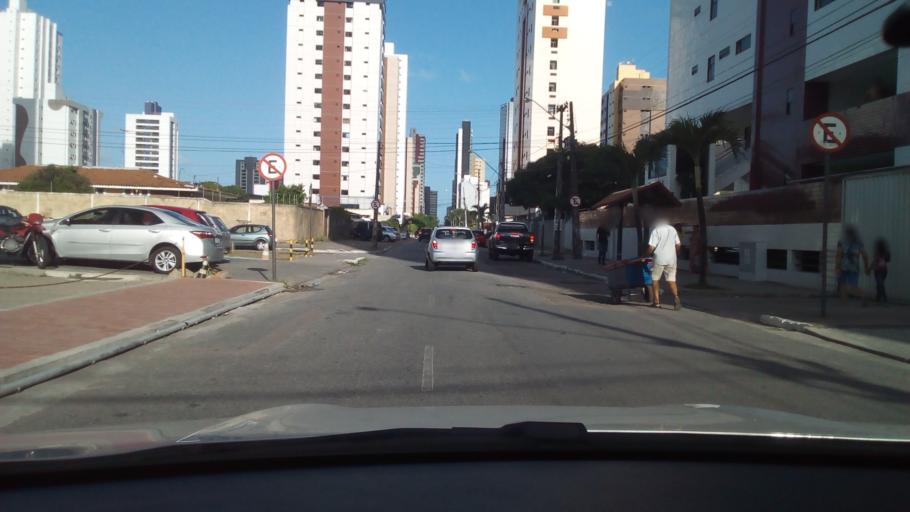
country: BR
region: Paraiba
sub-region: Joao Pessoa
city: Joao Pessoa
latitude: -7.1000
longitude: -34.8438
